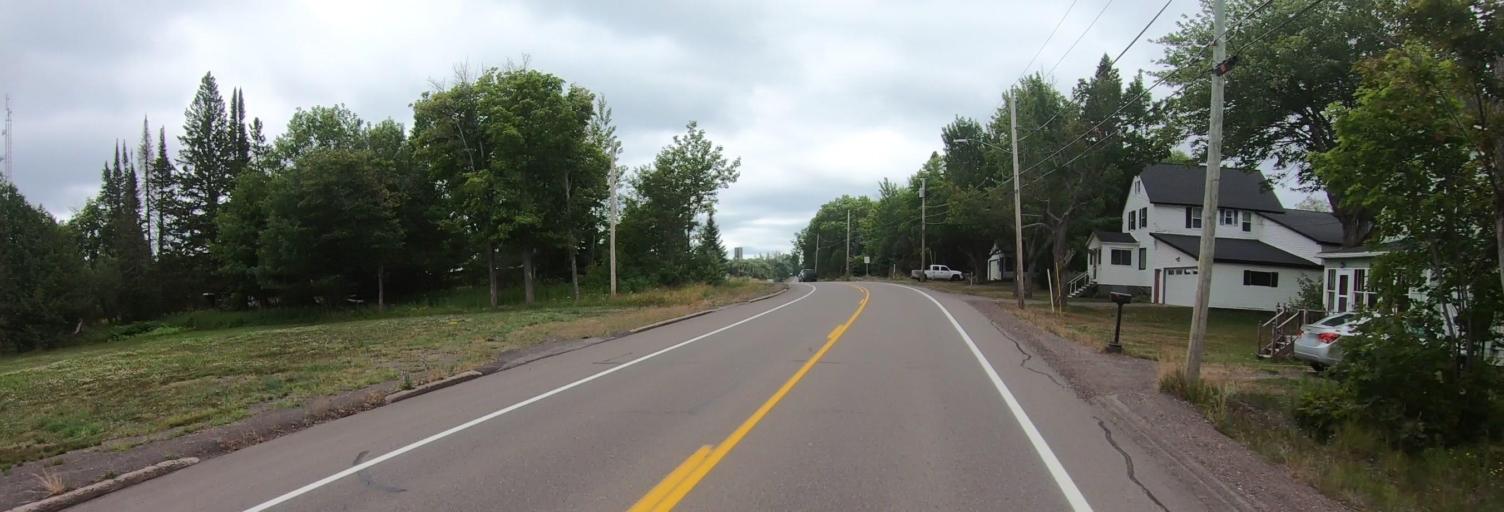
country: US
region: Michigan
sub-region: Houghton County
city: Laurium
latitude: 47.2661
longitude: -88.4236
